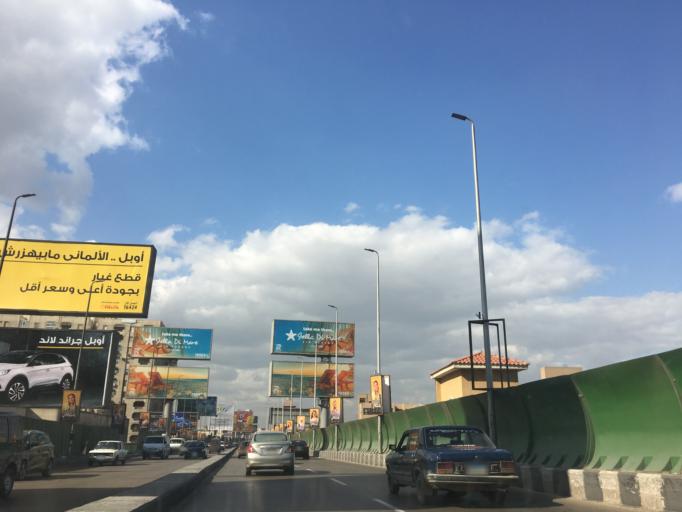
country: EG
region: Muhafazat al Qahirah
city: Cairo
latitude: 30.0721
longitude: 31.2892
